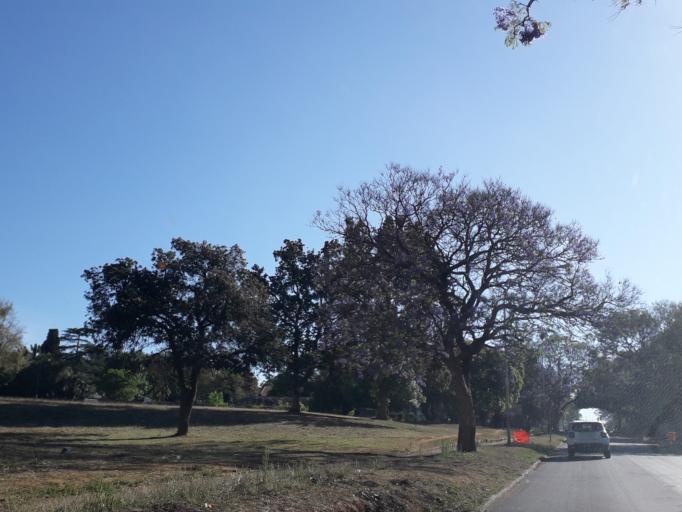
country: ZA
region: Gauteng
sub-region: City of Johannesburg Metropolitan Municipality
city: Roodepoort
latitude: -26.1350
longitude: 27.9639
